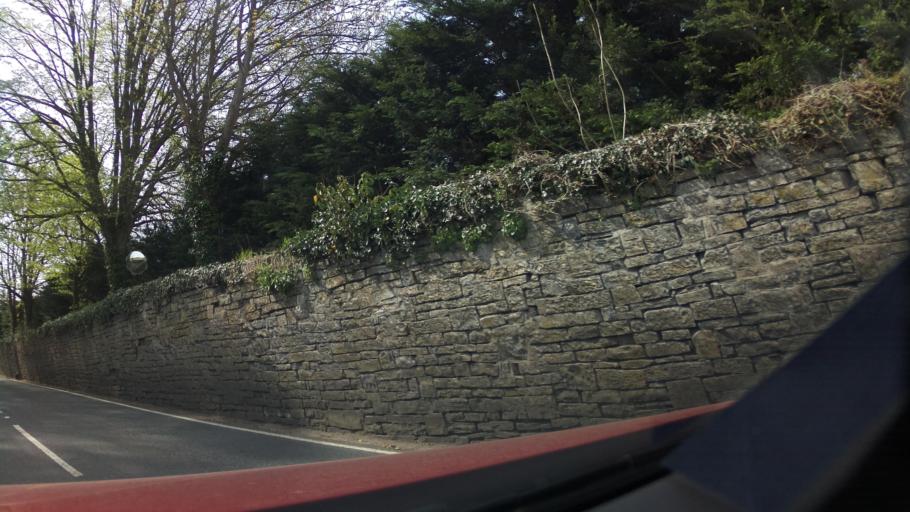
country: GB
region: England
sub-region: Somerset
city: Ilchester
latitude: 51.0506
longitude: -2.7174
